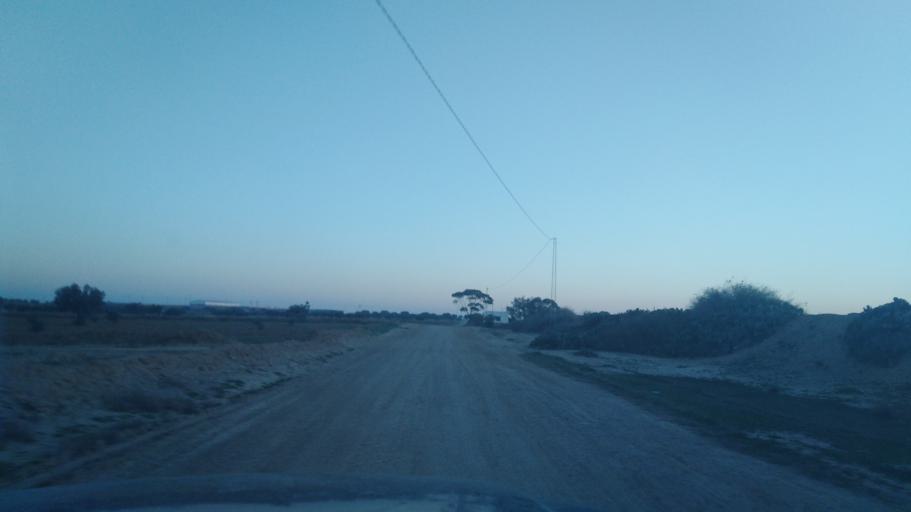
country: TN
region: Safaqis
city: Sfax
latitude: 34.7304
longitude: 10.4455
